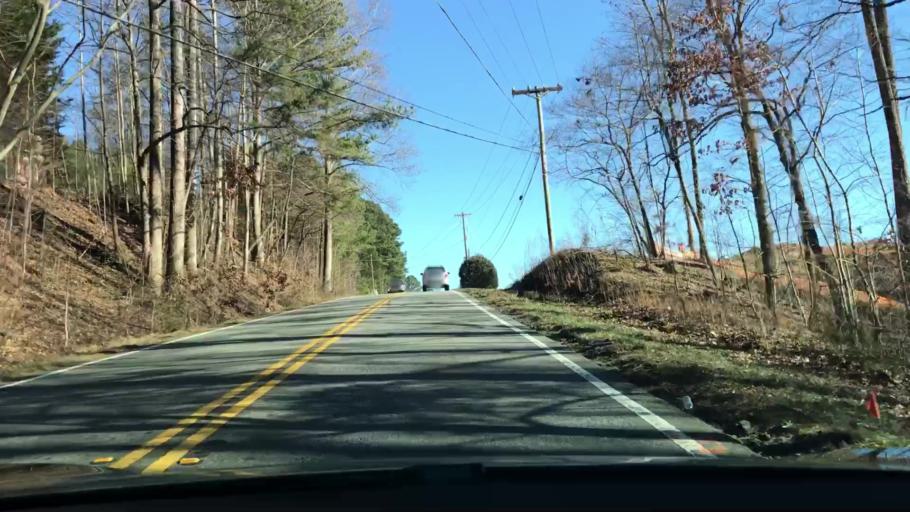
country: US
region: Georgia
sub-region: Forsyth County
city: Cumming
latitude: 34.1828
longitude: -84.0991
